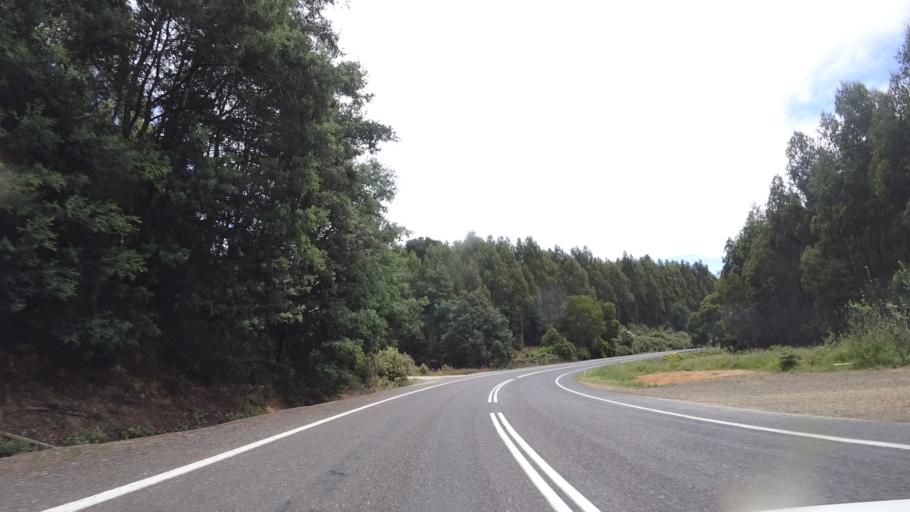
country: AU
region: Tasmania
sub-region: Dorset
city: Scottsdale
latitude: -41.1890
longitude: 147.6603
